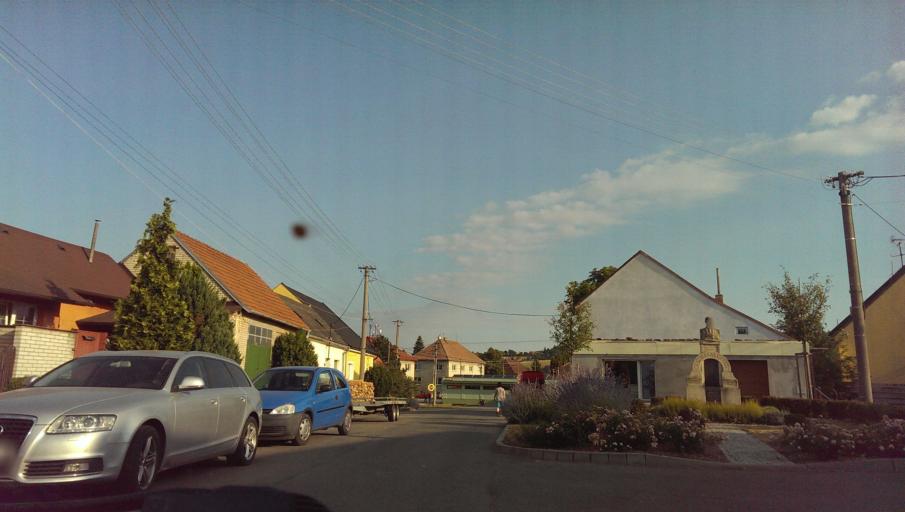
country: CZ
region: South Moravian
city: Zeravice
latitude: 49.0505
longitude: 17.2707
